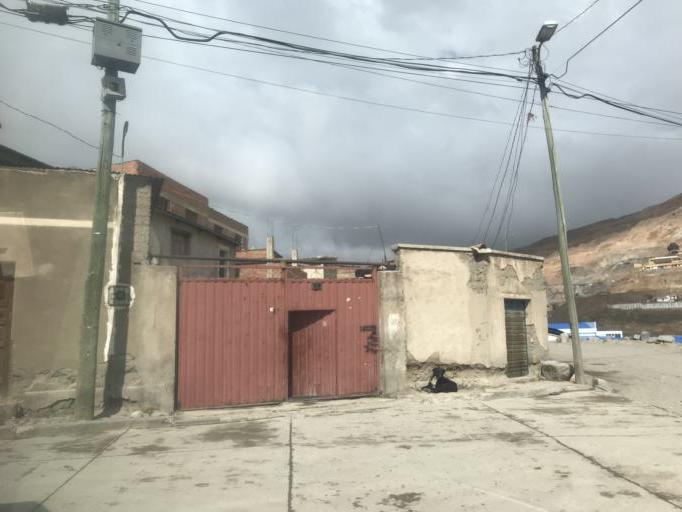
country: BO
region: Potosi
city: Potosi
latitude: -19.6020
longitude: -65.7451
